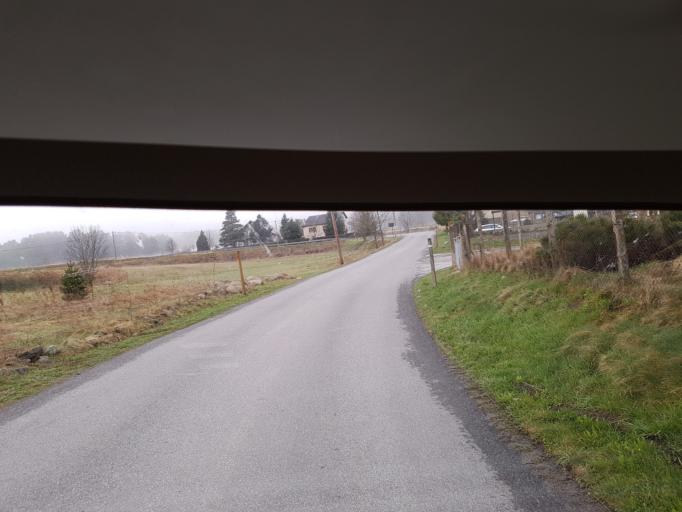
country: ES
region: Catalonia
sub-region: Provincia de Girona
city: Llivia
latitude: 42.6119
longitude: 2.1052
